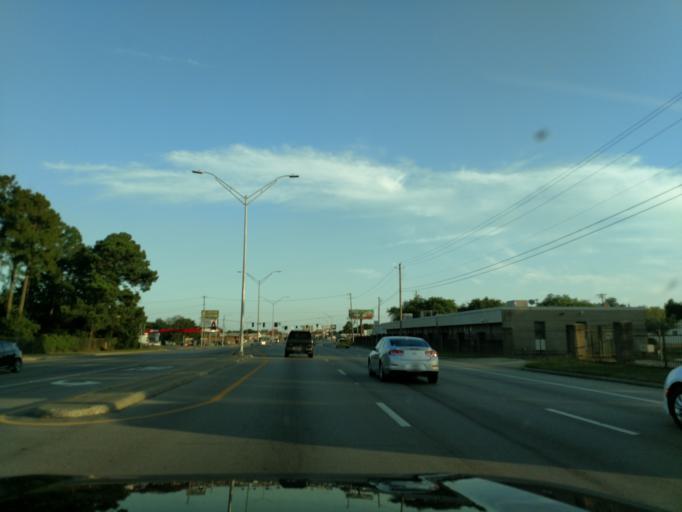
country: US
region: Mississippi
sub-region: Harrison County
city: West Gulfport
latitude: 30.3928
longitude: -89.0932
